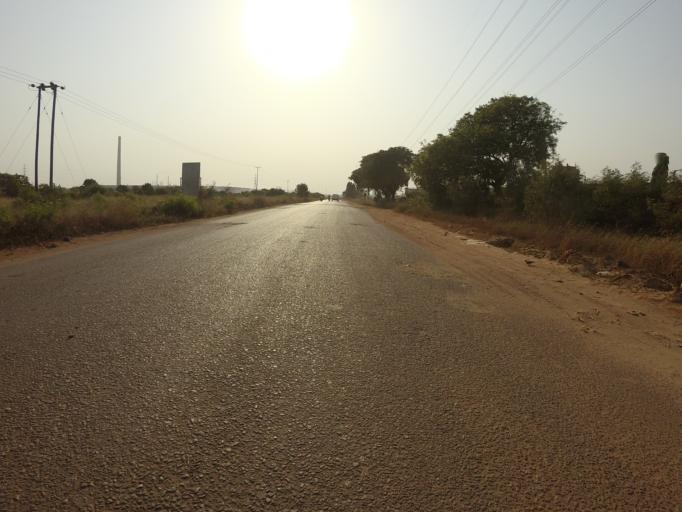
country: GH
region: Greater Accra
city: Tema
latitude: 5.6746
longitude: 0.0288
